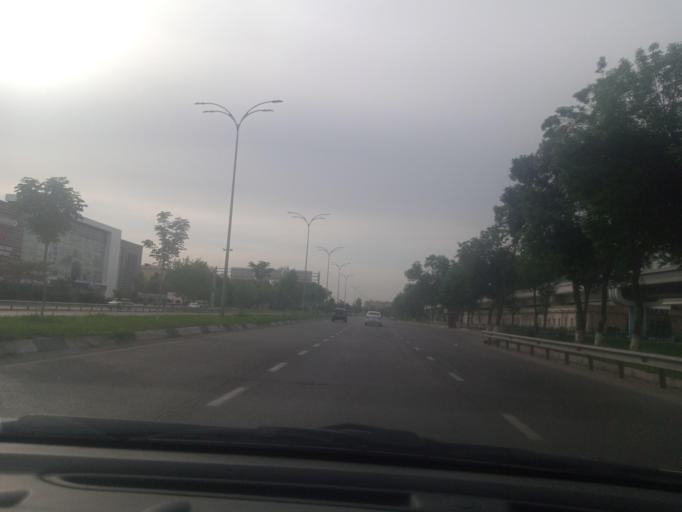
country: UZ
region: Toshkent
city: Salor
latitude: 41.2991
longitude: 69.3482
